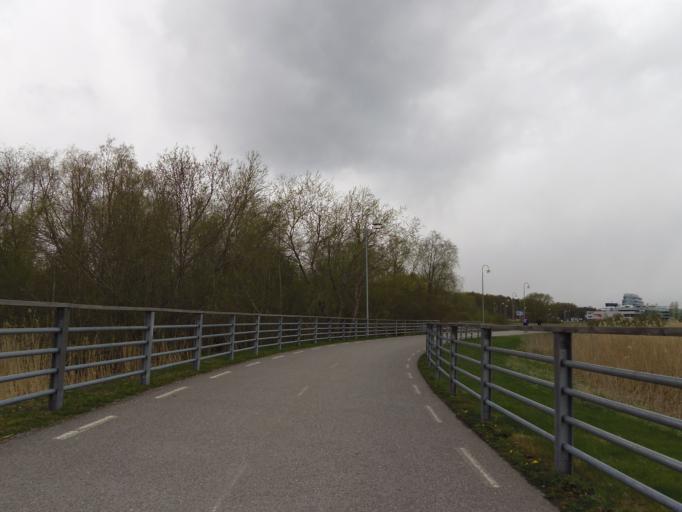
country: EE
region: Harju
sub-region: Tallinna linn
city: Tallinn
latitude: 59.4297
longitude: 24.6721
